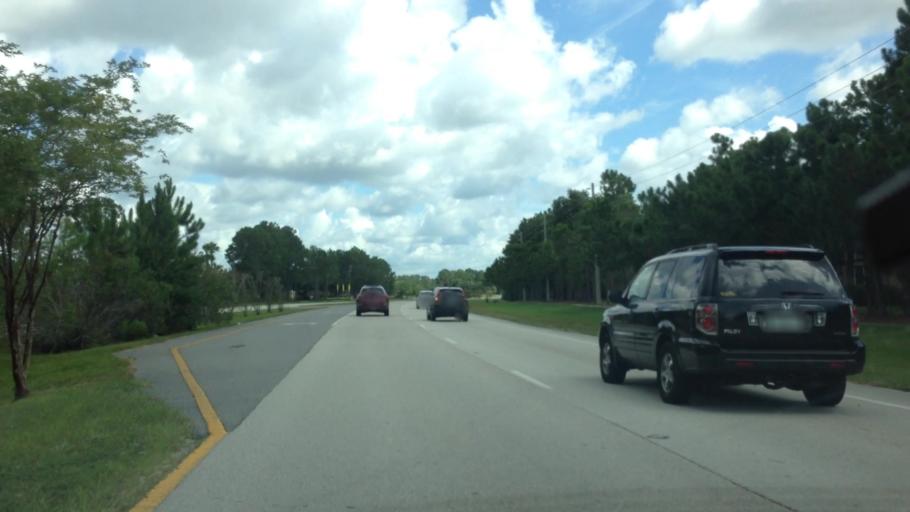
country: US
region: Florida
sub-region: Duval County
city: Jacksonville Beach
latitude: 30.2596
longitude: -81.4666
